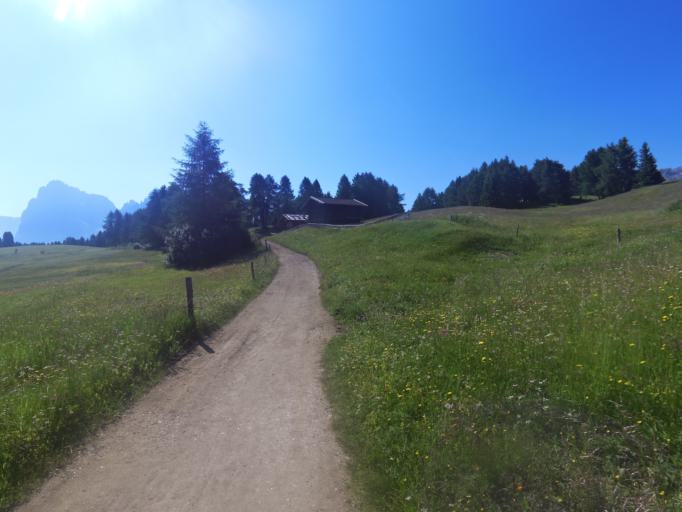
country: IT
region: Trentino-Alto Adige
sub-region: Bolzano
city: Ortisei
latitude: 46.5373
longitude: 11.6424
